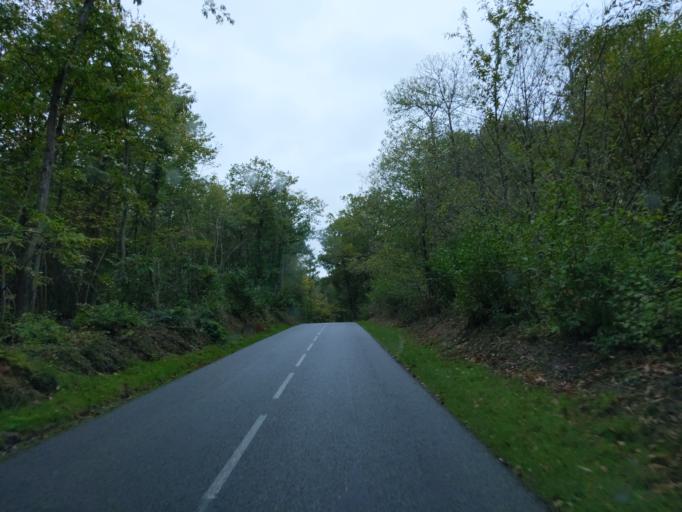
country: FR
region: Ile-de-France
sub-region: Departement des Yvelines
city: Bullion
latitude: 48.6267
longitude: 1.9725
